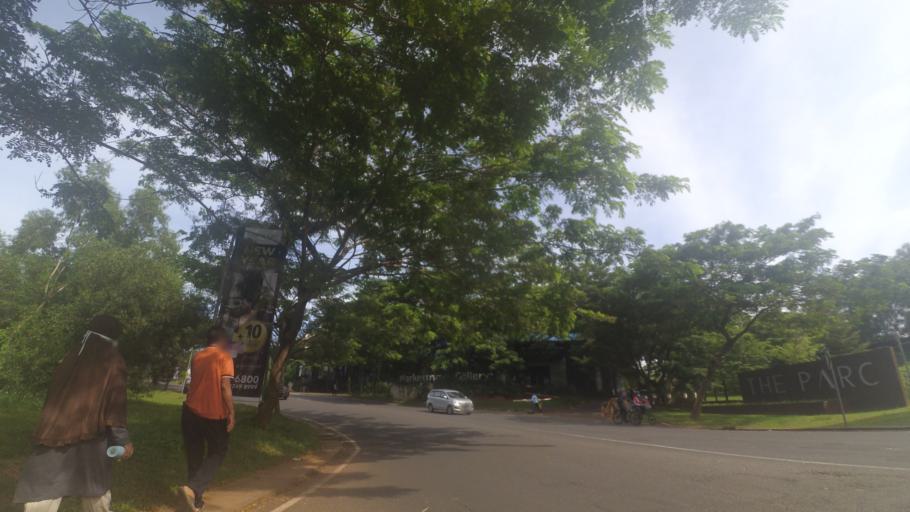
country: ID
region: West Java
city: Pamulang
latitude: -6.3426
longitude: 106.7709
